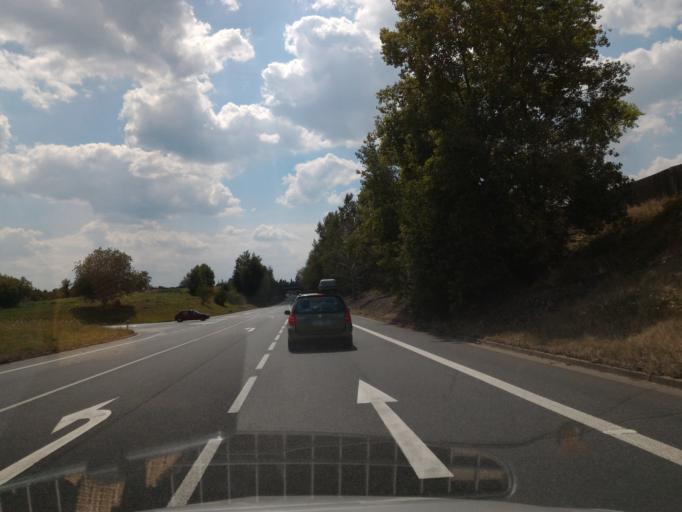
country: CZ
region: Central Bohemia
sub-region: Okres Kutna Hora
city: Caslav
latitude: 49.9067
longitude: 15.4064
